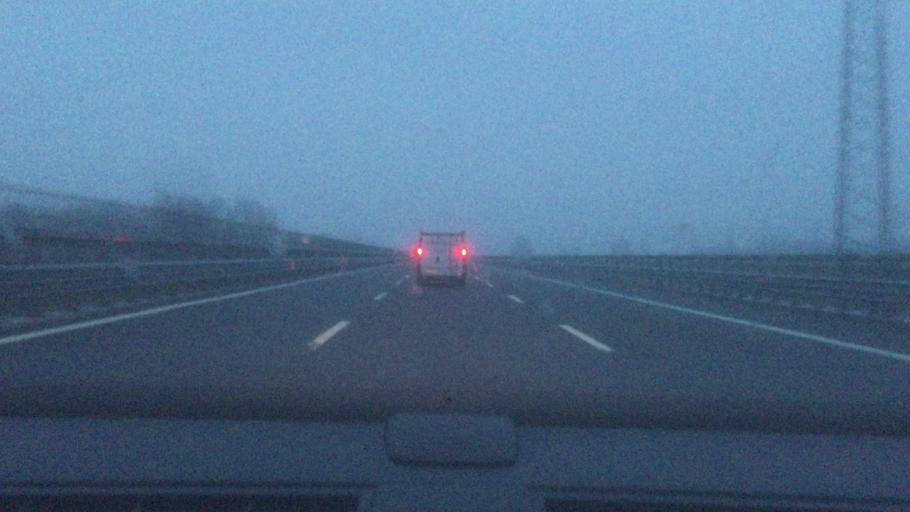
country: IT
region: Lombardy
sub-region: Provincia di Bergamo
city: Bariano
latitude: 45.4975
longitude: 9.7184
